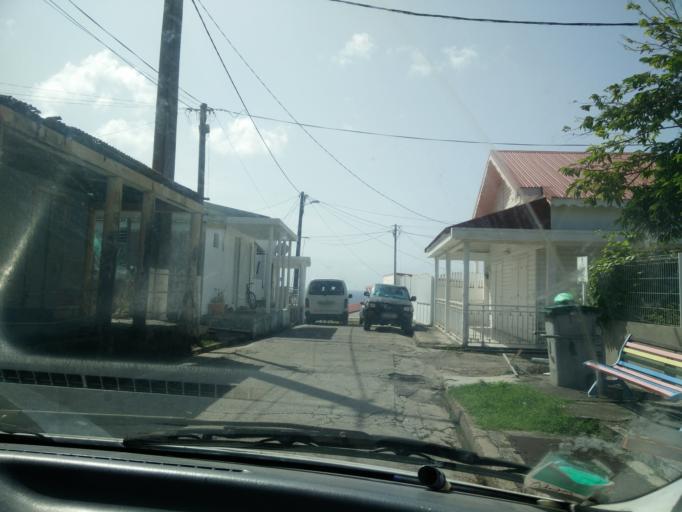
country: GP
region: Guadeloupe
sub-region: Guadeloupe
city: Terre-de-Bas
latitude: 15.8500
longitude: -61.6464
